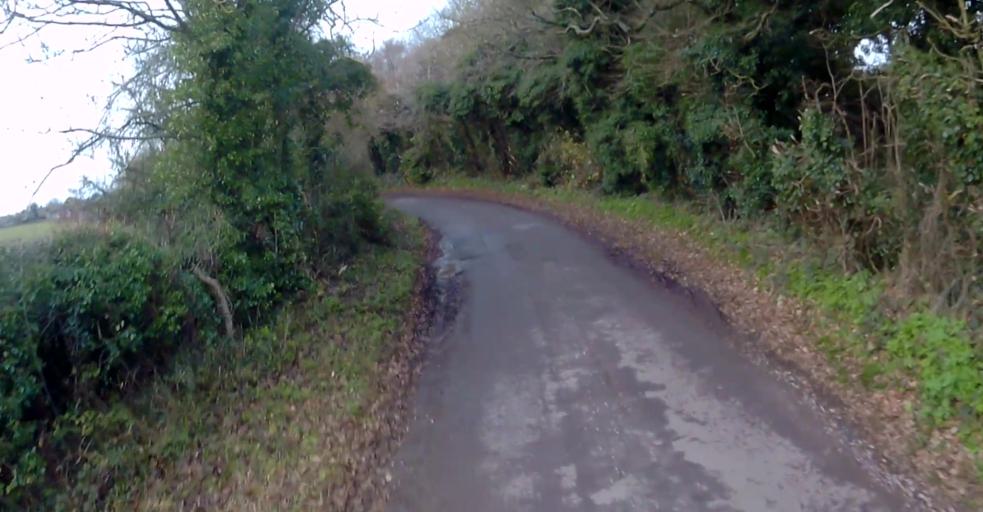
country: GB
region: England
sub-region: Hampshire
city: Overton
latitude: 51.2378
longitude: -1.2546
